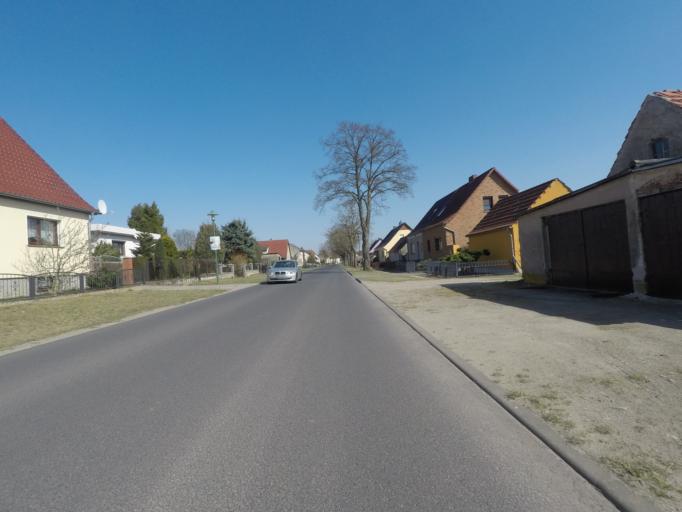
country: DE
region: Brandenburg
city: Britz
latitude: 52.8679
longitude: 13.7330
